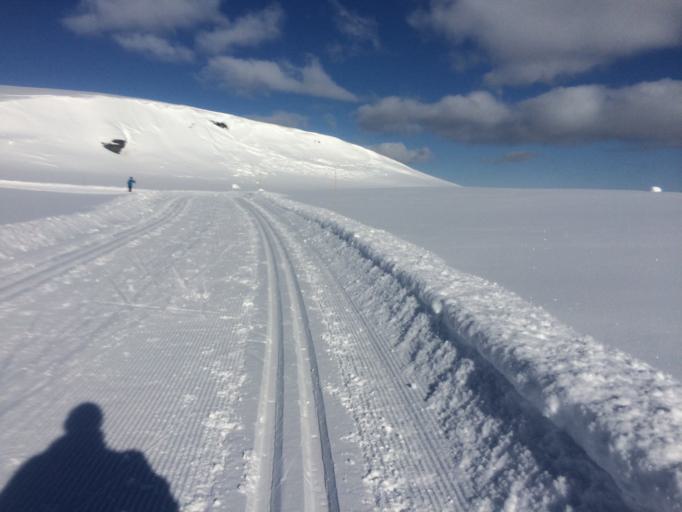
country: NO
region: Oppland
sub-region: Ringebu
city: Ringebu
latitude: 61.3693
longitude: 10.0764
